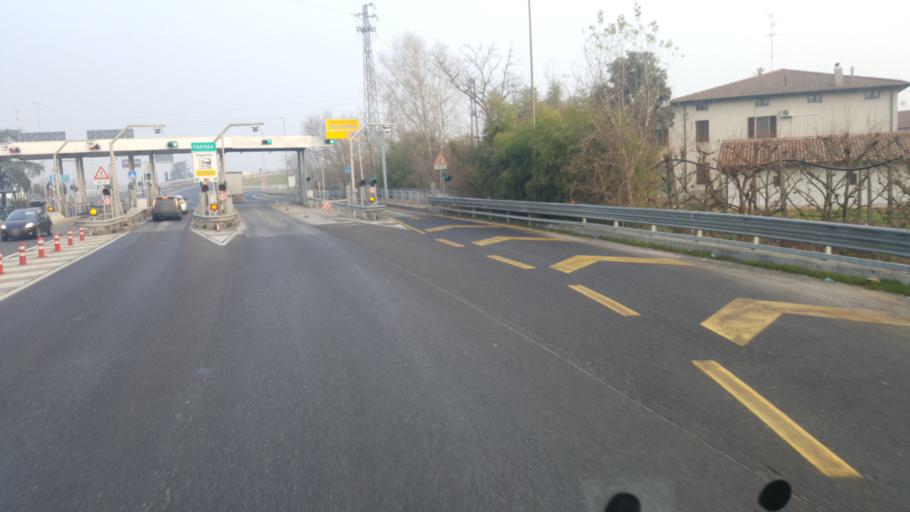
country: IT
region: Emilia-Romagna
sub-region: Provincia di Ravenna
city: Faenza
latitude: 44.3216
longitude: 11.9042
